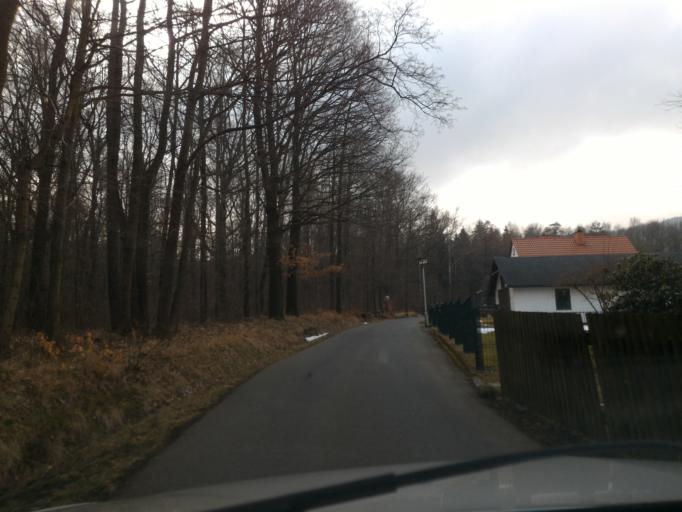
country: DE
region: Saxony
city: Kurort Jonsdorf
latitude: 50.8617
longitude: 14.7253
